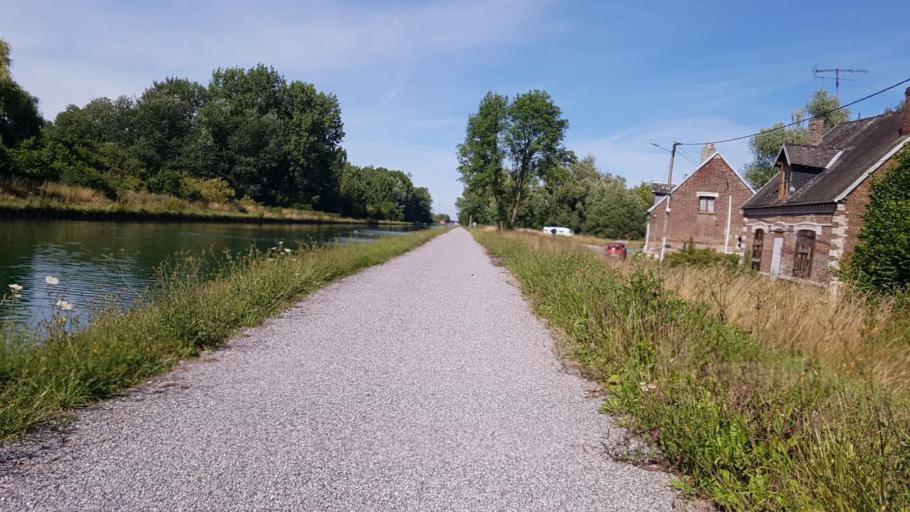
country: FR
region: Picardie
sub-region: Departement de l'Aisne
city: Viry-Noureuil
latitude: 49.6233
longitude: 3.2541
